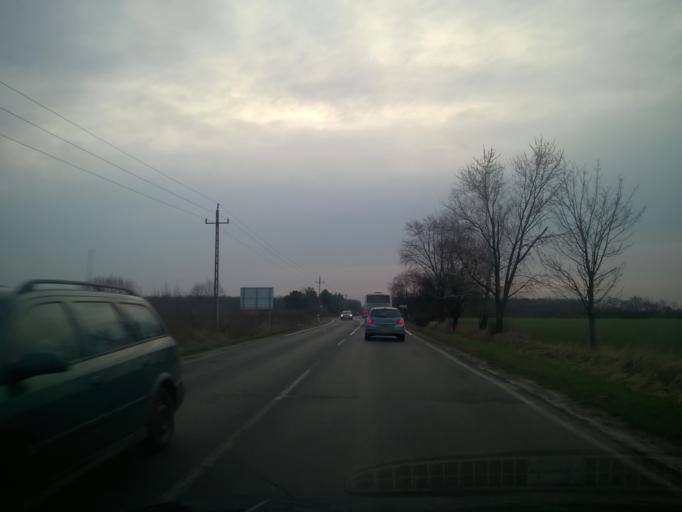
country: HU
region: Baranya
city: Szigetvar
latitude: 46.0489
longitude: 17.8456
